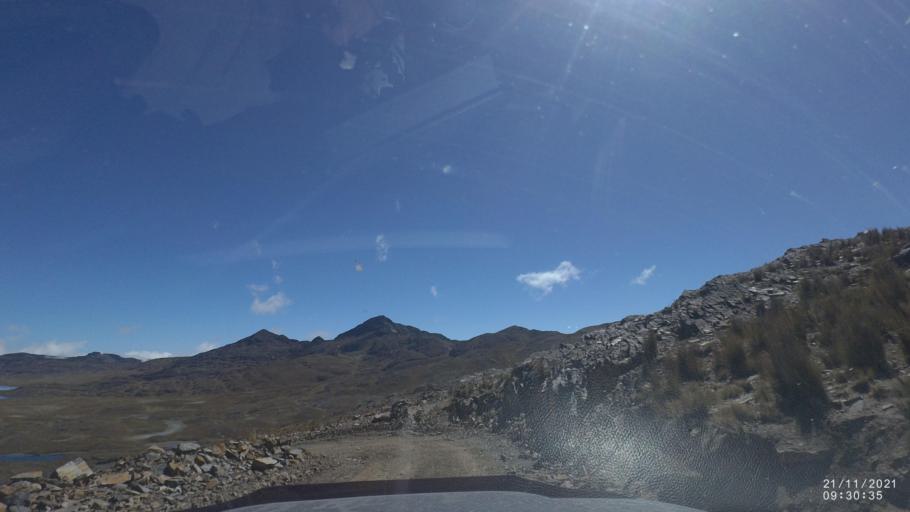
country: BO
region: Cochabamba
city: Cochabamba
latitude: -17.0757
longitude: -66.2559
